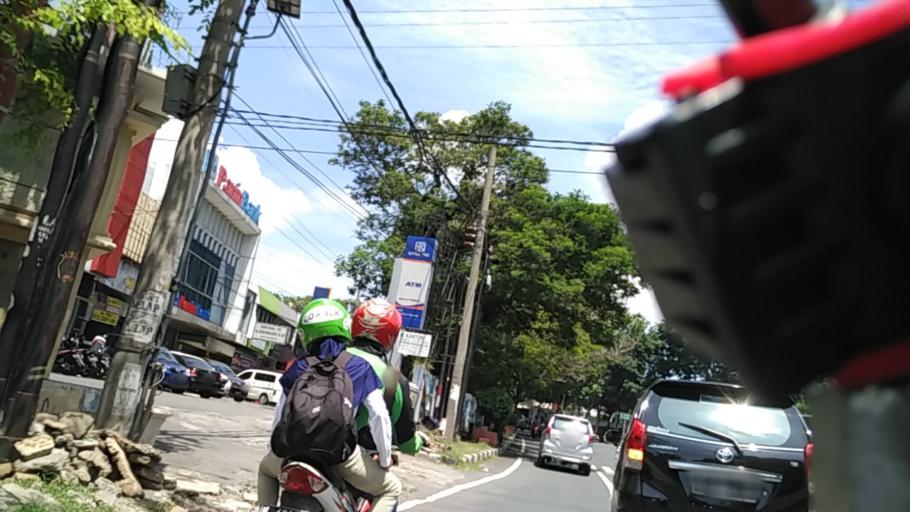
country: ID
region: Central Java
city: Semarang
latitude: -7.0086
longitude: 110.4161
